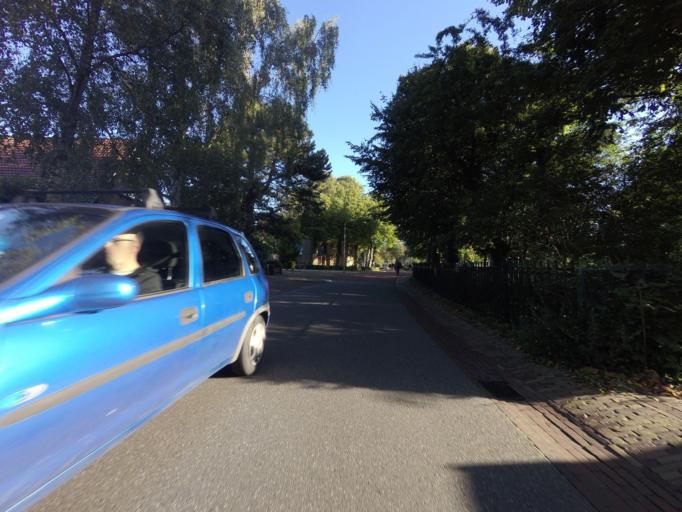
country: NL
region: North Holland
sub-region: Gemeente Langedijk
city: Broek op Langedijk
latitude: 52.6651
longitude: 4.7864
